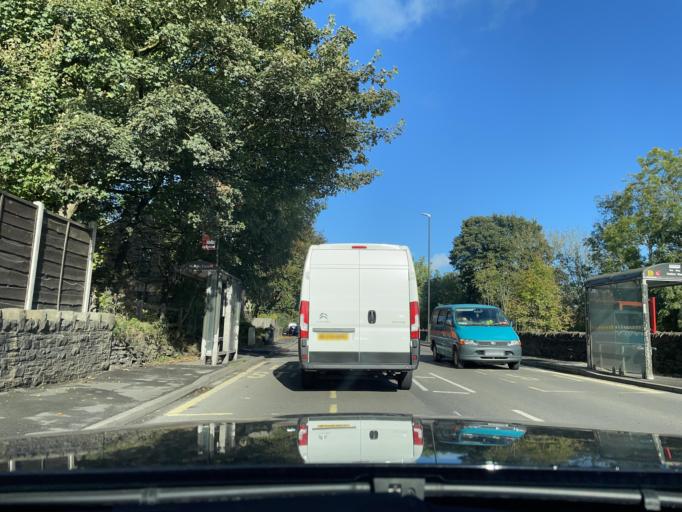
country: GB
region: England
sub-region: Derbyshire
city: Whaley Bridge
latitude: 53.3456
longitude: -1.9863
